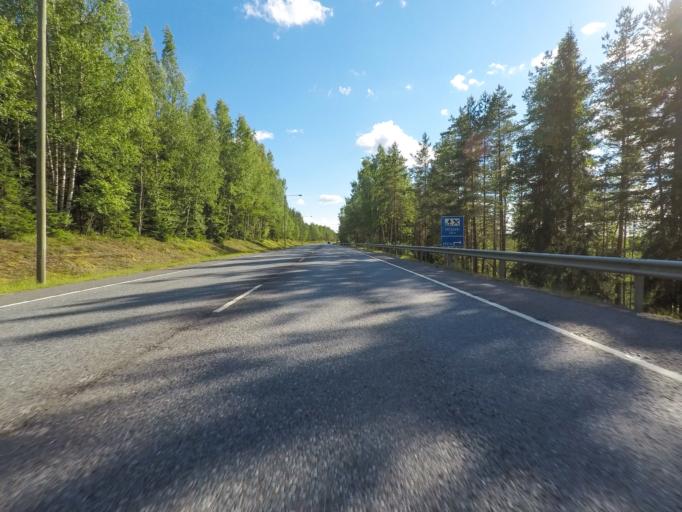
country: FI
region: Uusimaa
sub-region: Helsinki
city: Vihti
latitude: 60.3303
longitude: 24.2821
